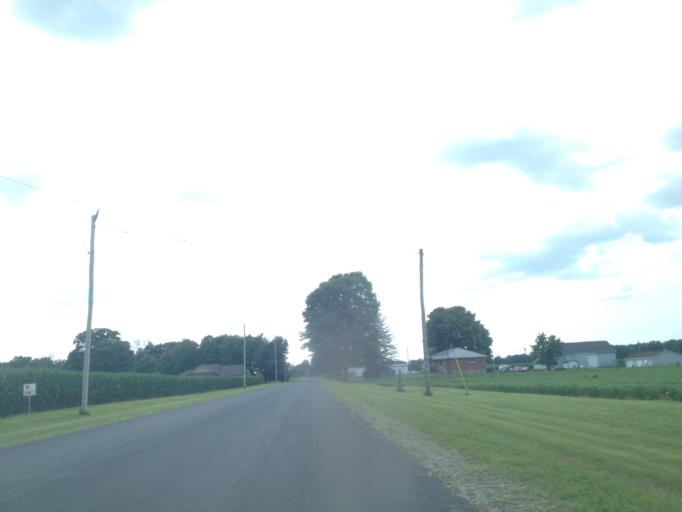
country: CA
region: Ontario
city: Aylmer
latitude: 42.6811
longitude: -81.0007
